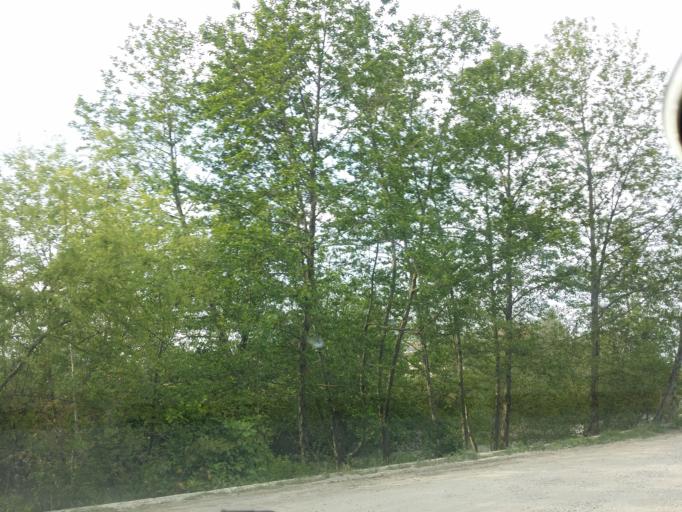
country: IR
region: Mazandaran
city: Chalus
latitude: 36.6844
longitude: 51.3965
